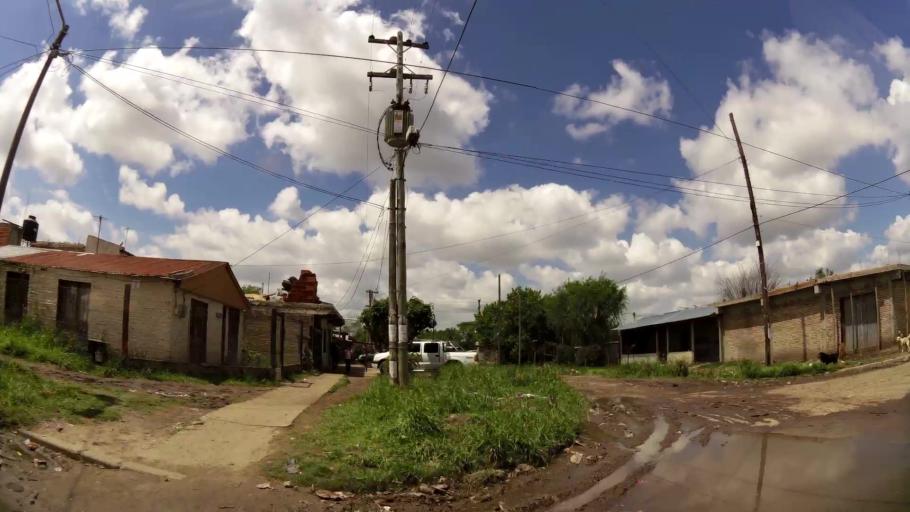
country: AR
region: Buenos Aires
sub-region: Partido de Quilmes
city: Quilmes
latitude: -34.8401
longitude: -58.2314
